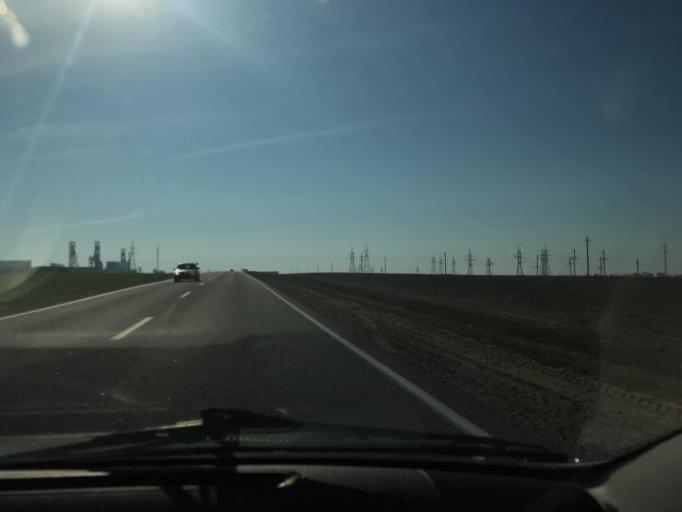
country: BY
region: Minsk
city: Salihorsk
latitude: 52.8650
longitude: 27.4670
